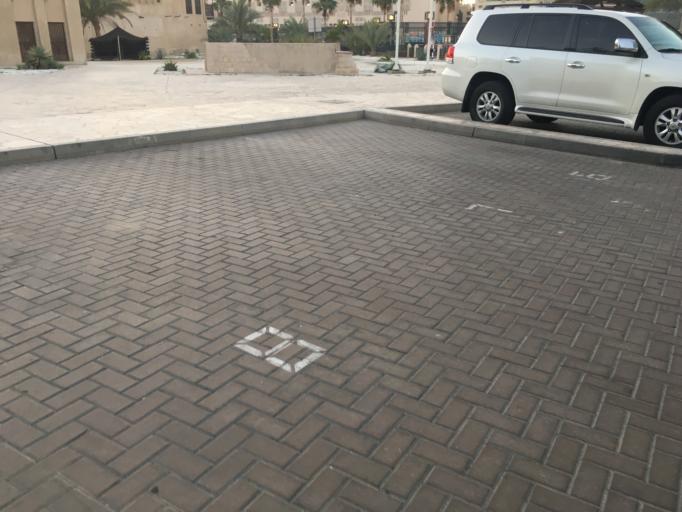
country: AE
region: Ash Shariqah
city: Sharjah
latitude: 25.2645
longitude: 55.3008
